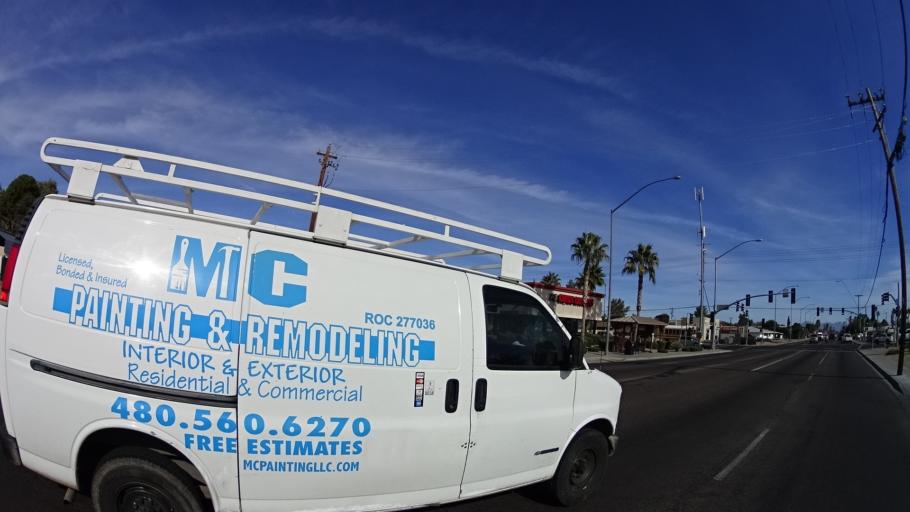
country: US
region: Arizona
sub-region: Maricopa County
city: Mesa
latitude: 33.4077
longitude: -111.8063
